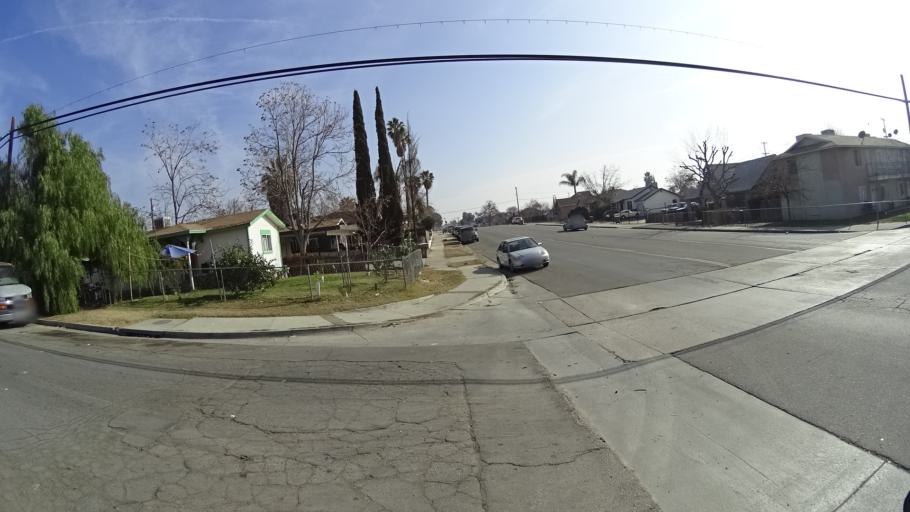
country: US
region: California
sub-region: Kern County
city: Bakersfield
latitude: 35.3834
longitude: -118.9773
